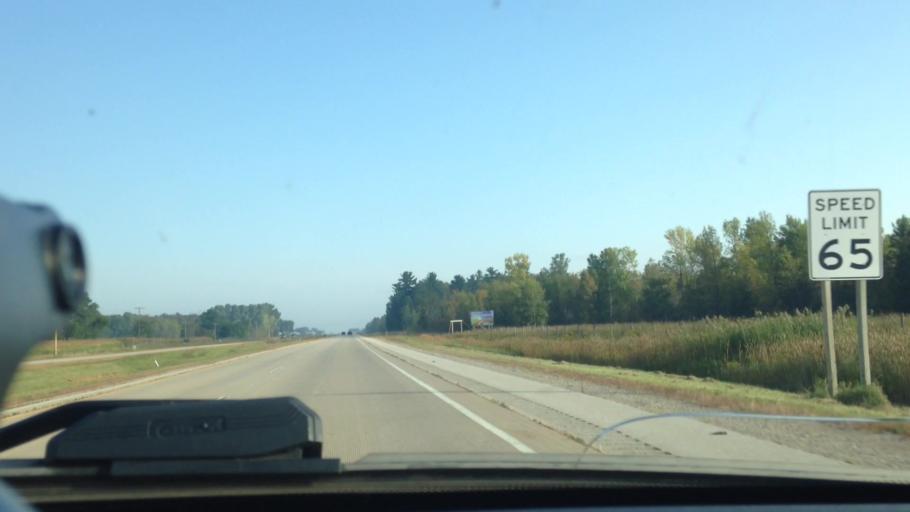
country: US
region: Wisconsin
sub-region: Oconto County
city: Oconto Falls
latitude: 45.0234
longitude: -88.0449
